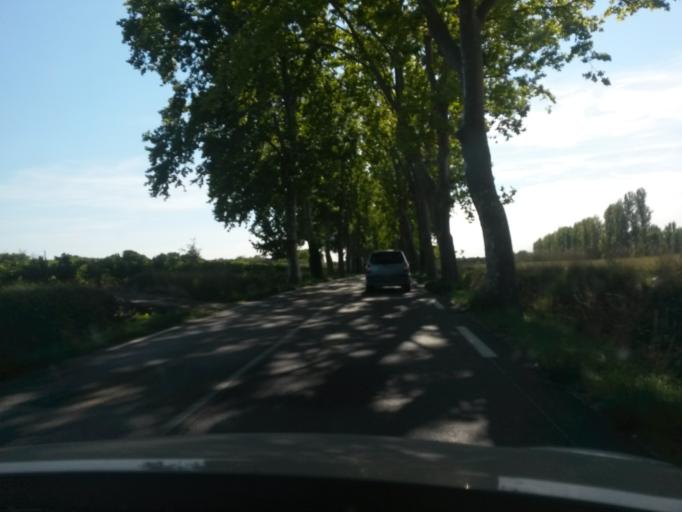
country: FR
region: Languedoc-Roussillon
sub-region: Departement de l'Herault
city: Gignac
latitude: 43.6622
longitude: 3.5637
